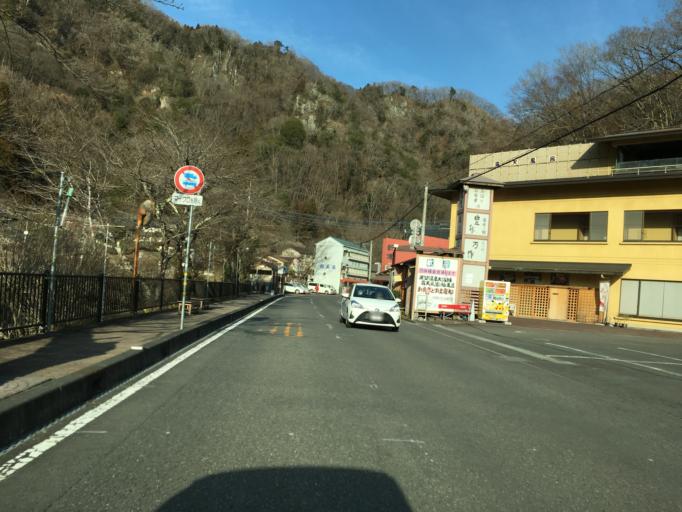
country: JP
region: Ibaraki
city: Daigo
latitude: 36.7642
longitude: 140.4001
